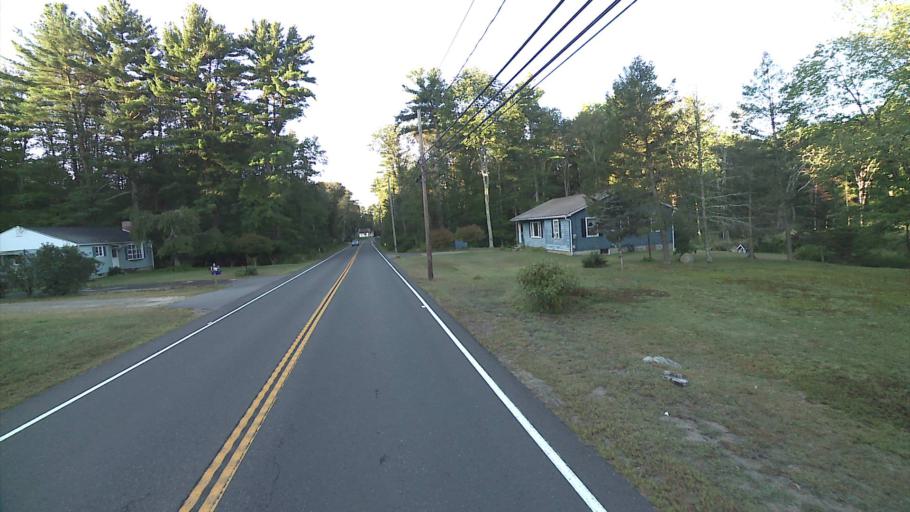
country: US
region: Connecticut
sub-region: Tolland County
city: Stafford
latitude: 41.9927
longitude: -72.3157
